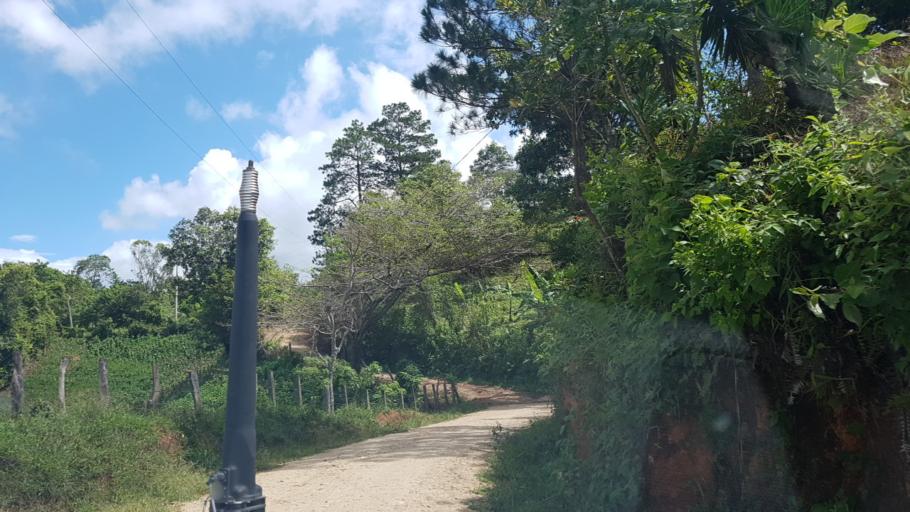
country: NI
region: Nueva Segovia
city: Ciudad Antigua
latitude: 13.6507
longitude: -86.2500
